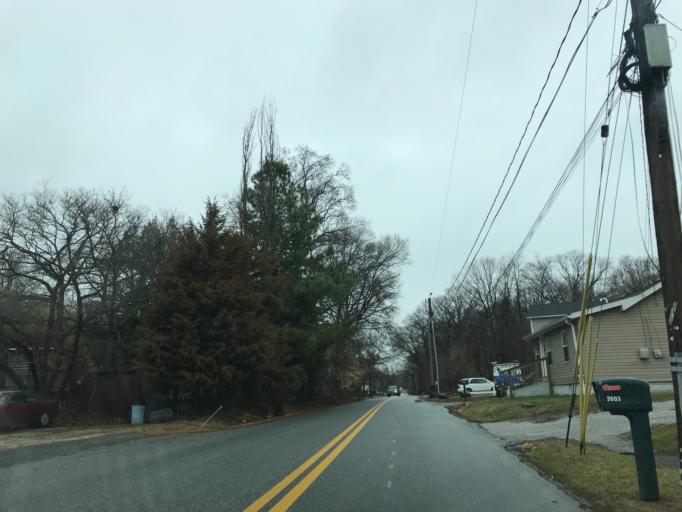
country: US
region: Maryland
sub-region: Baltimore County
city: Edgemere
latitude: 39.2310
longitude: -76.4466
